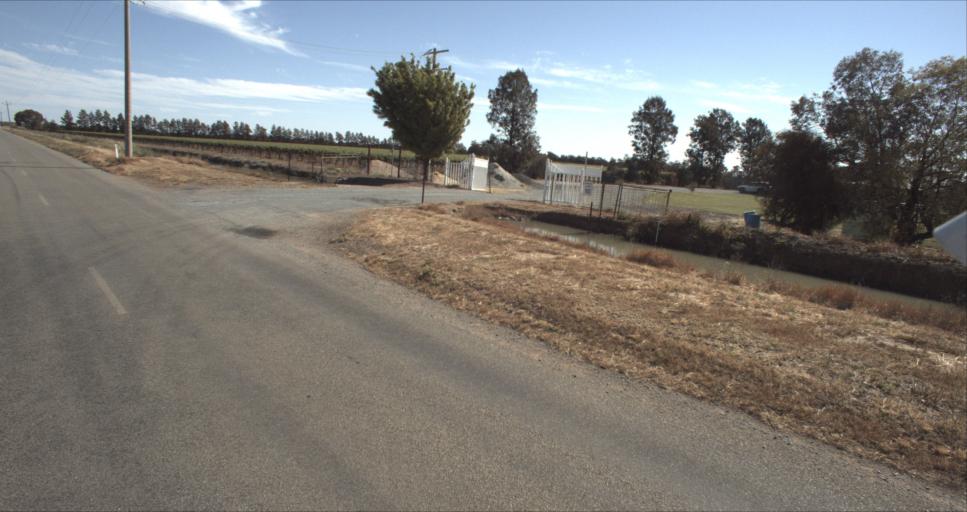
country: AU
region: New South Wales
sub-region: Leeton
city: Leeton
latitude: -34.5811
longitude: 146.3798
